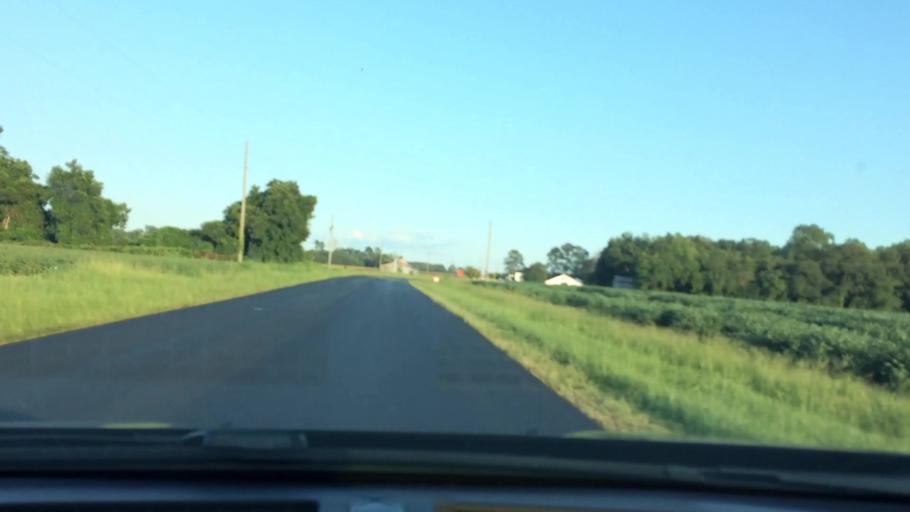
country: US
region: North Carolina
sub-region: Pitt County
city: Ayden
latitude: 35.4475
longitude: -77.4615
